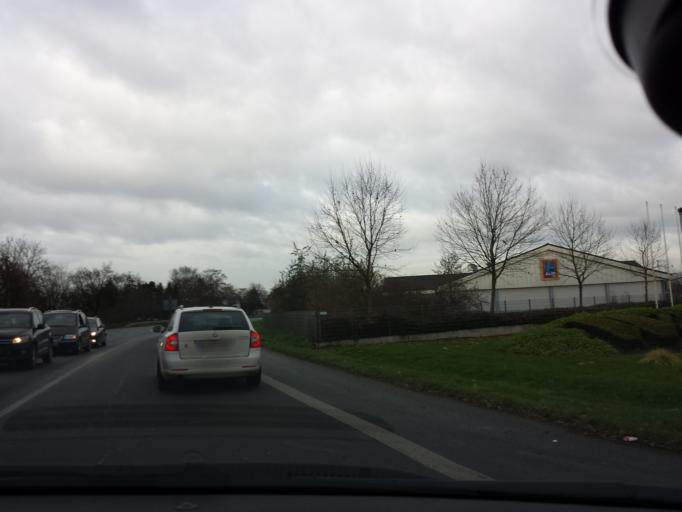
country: DE
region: North Rhine-Westphalia
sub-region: Regierungsbezirk Dusseldorf
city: Weeze
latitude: 51.6201
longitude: 6.2092
